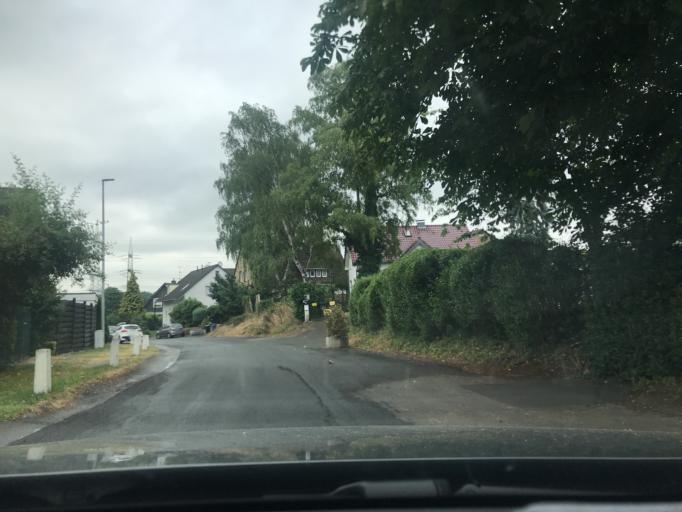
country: DE
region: North Rhine-Westphalia
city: Haan
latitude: 51.1705
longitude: 6.9864
